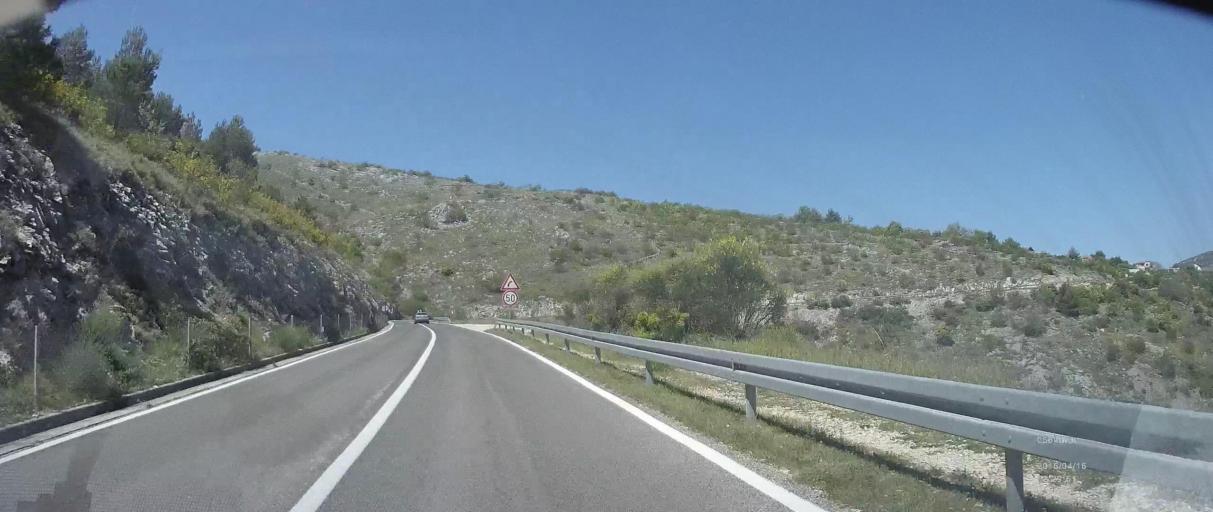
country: HR
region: Splitsko-Dalmatinska
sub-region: Grad Trogir
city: Trogir
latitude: 43.5268
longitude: 16.2186
